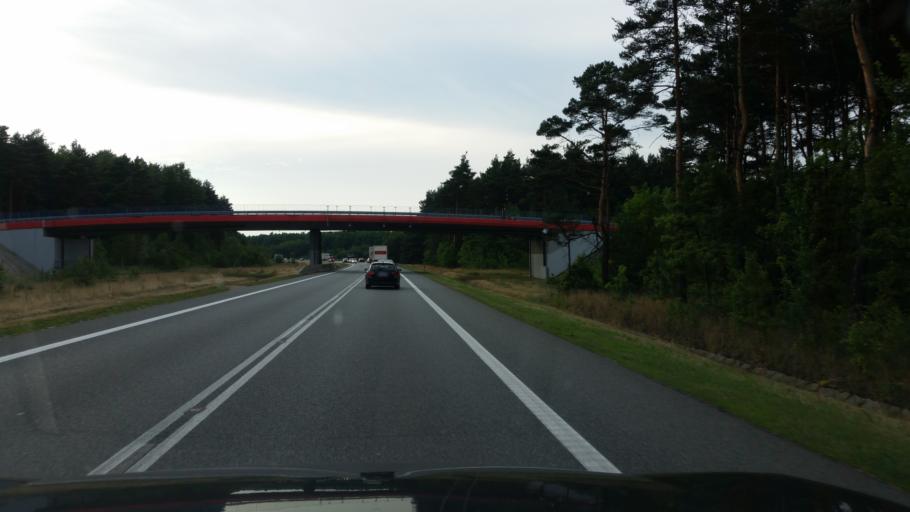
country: PL
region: Silesian Voivodeship
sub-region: Powiat bedzinski
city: Mierzecice
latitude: 50.4533
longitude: 19.1089
